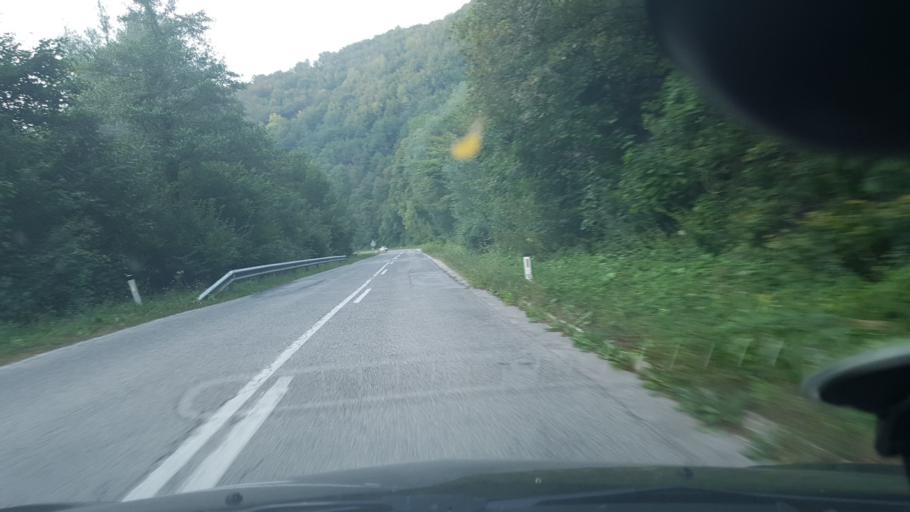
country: SI
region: Kozje
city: Kozje
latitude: 46.0603
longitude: 15.5688
